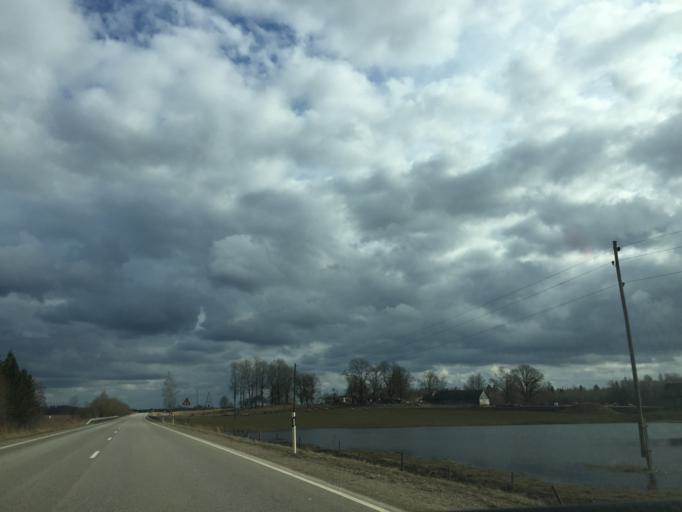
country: LV
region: Lielvarde
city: Lielvarde
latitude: 56.4993
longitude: 24.7518
